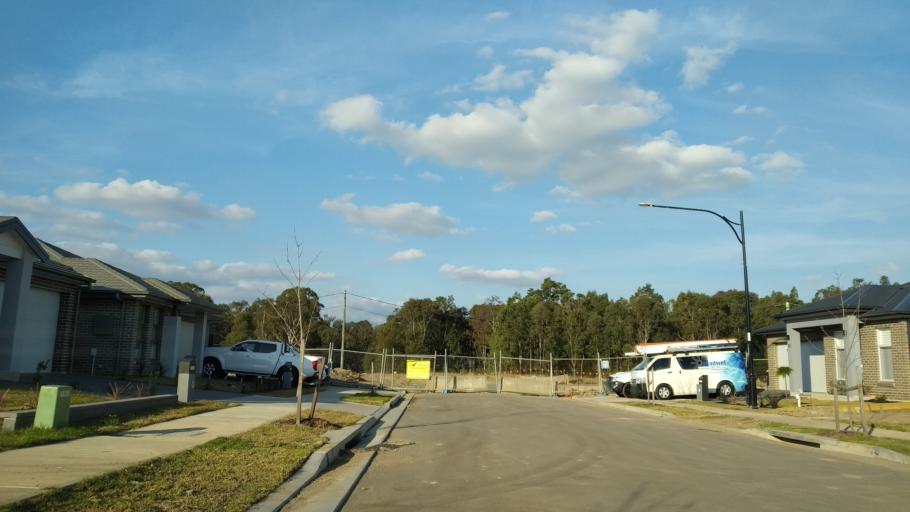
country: AU
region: New South Wales
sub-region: Penrith Municipality
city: Werrington County
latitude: -33.7291
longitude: 150.7568
